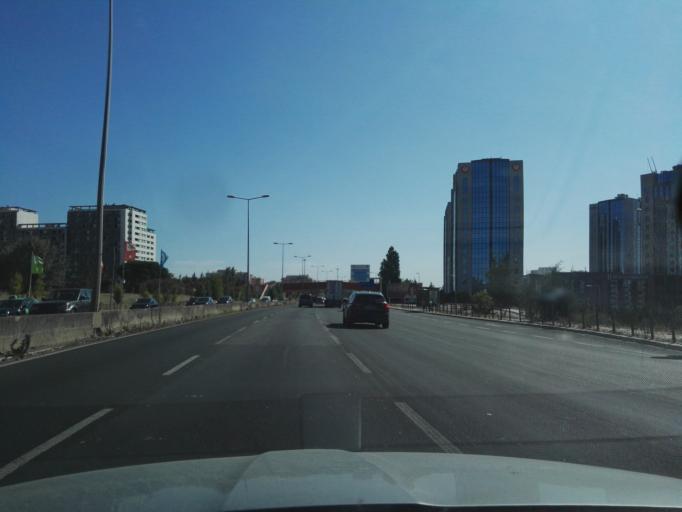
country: PT
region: Lisbon
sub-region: Odivelas
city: Pontinha
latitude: 38.7573
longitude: -9.1782
